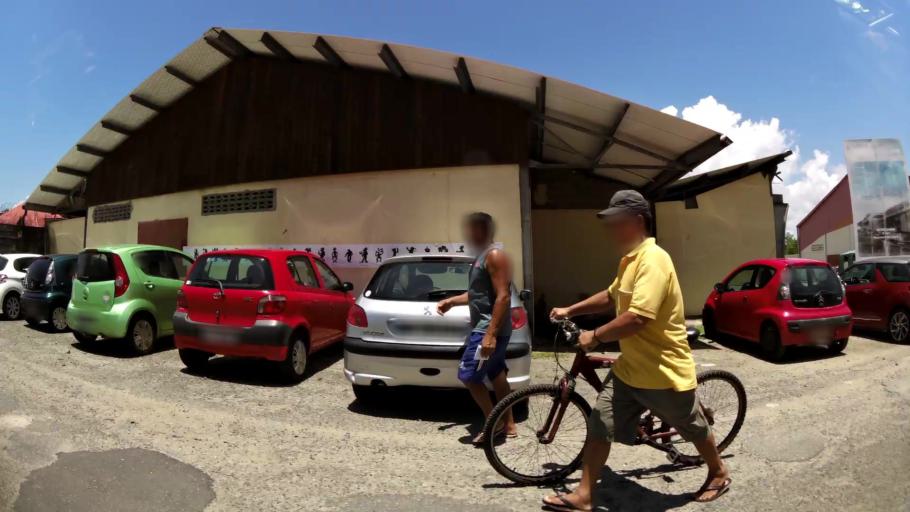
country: GF
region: Guyane
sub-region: Guyane
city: Cayenne
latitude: 4.9364
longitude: -52.3369
